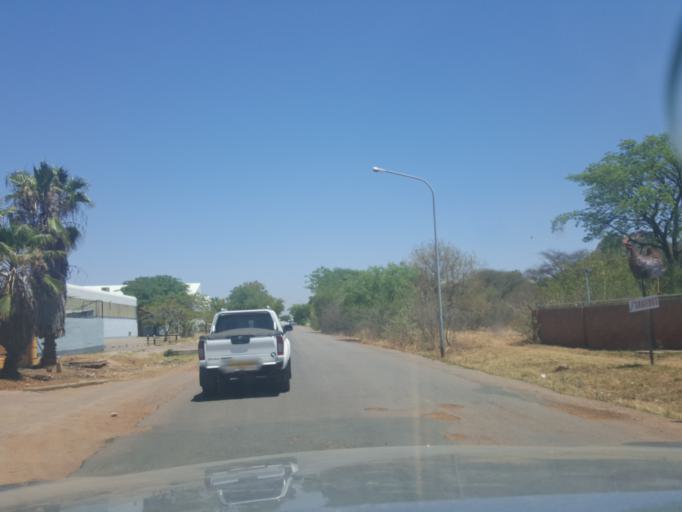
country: BW
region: South East
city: Gaborone
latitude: -24.6853
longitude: 25.8889
